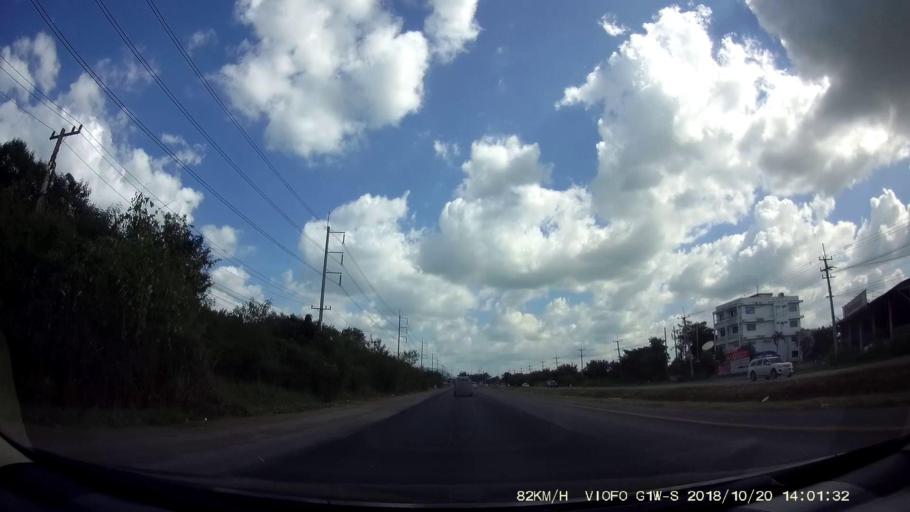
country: TH
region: Khon Kaen
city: Chum Phae
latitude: 16.5014
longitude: 102.1213
